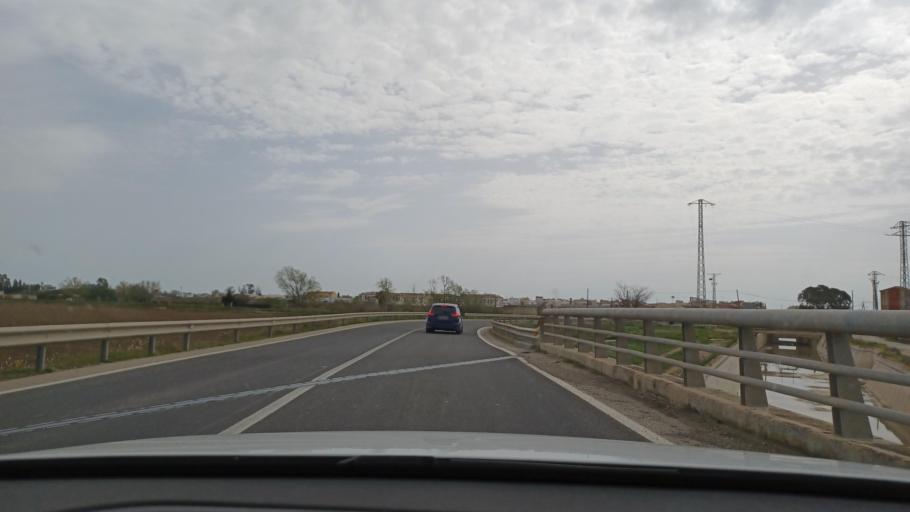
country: ES
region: Catalonia
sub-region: Provincia de Tarragona
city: Deltebre
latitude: 40.7058
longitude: 0.7065
